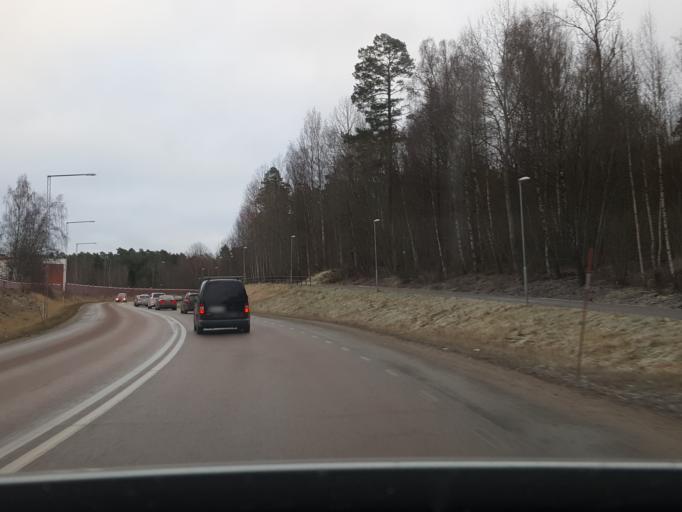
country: SE
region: Stockholm
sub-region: Botkyrka Kommun
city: Alby
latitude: 59.2353
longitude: 17.8385
